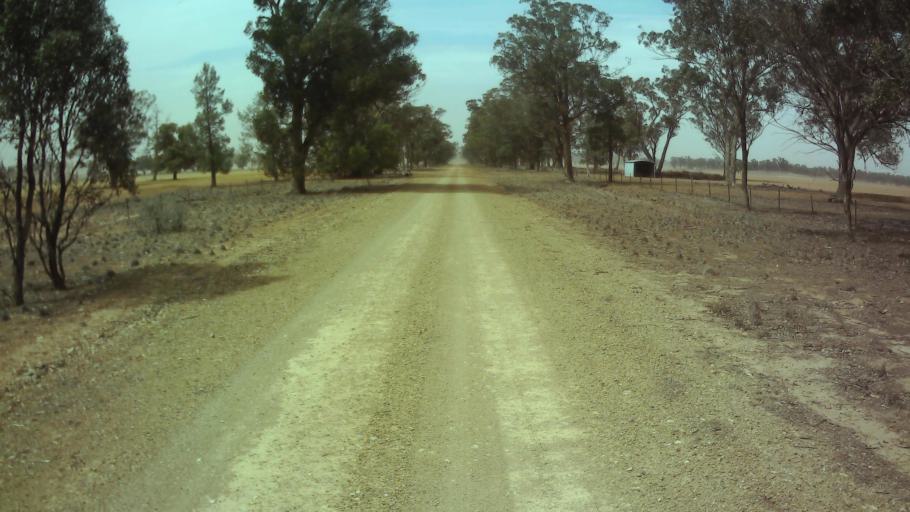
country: AU
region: New South Wales
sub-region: Weddin
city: Grenfell
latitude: -33.7308
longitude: 147.9629
